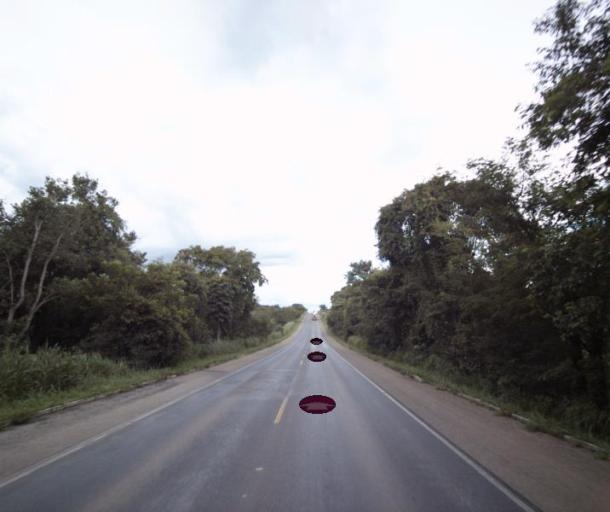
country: BR
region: Goias
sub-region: Itapaci
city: Itapaci
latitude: -15.0312
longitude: -49.4328
